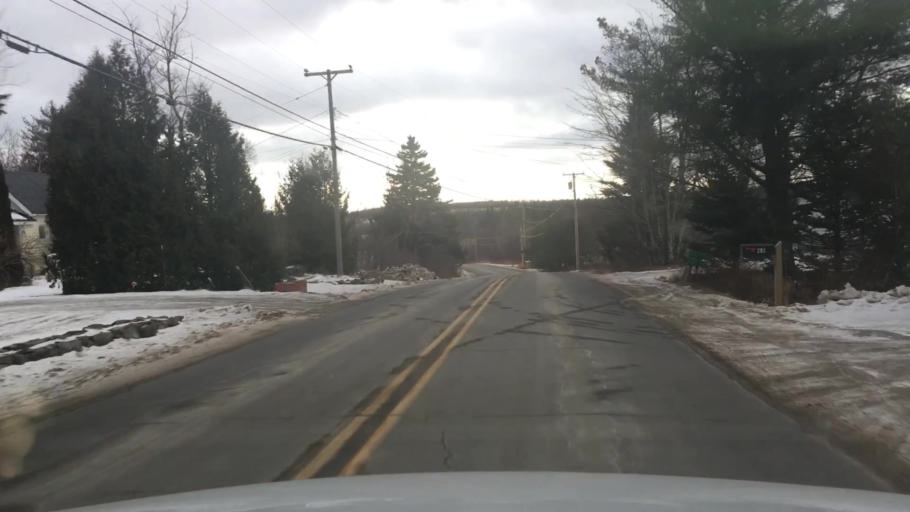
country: US
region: Maine
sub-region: Washington County
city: Machias
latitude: 44.6852
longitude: -67.4664
